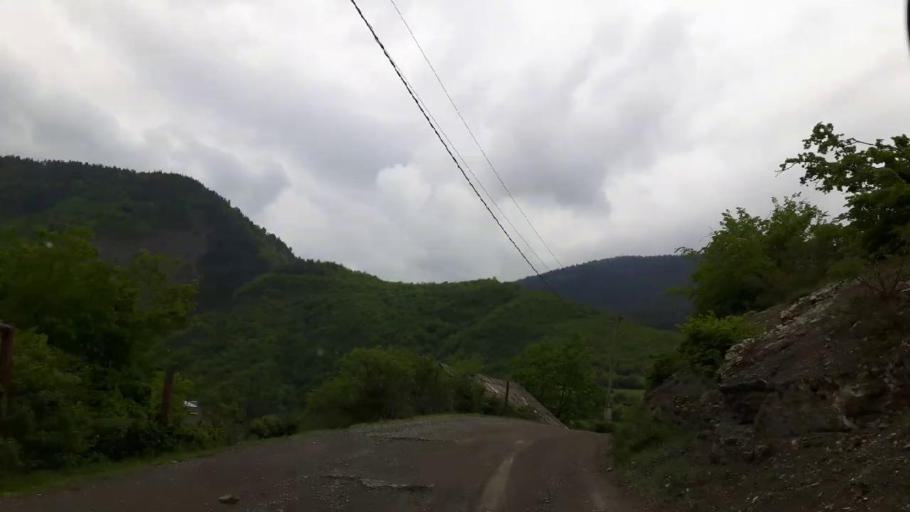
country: GE
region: Shida Kartli
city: Gori
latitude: 41.8900
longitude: 44.0056
